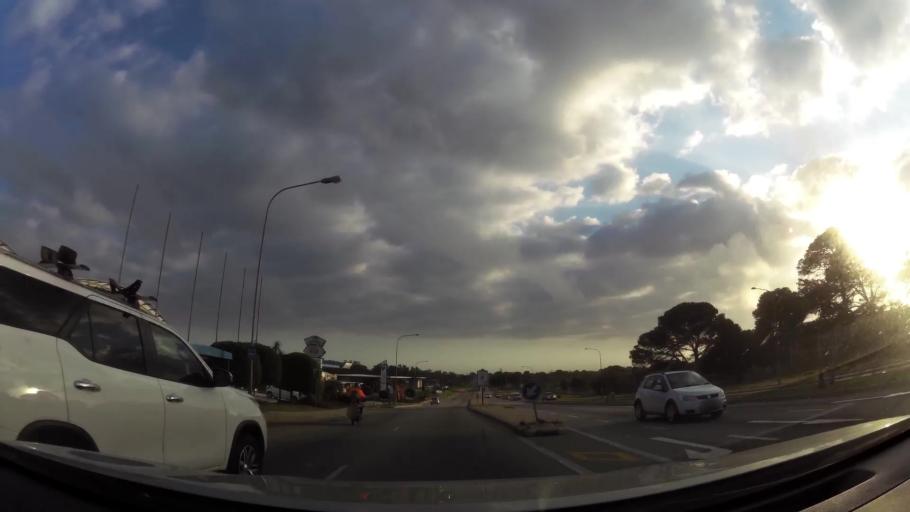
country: ZA
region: Eastern Cape
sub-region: Nelson Mandela Bay Metropolitan Municipality
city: Port Elizabeth
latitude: -33.9811
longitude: 25.5531
